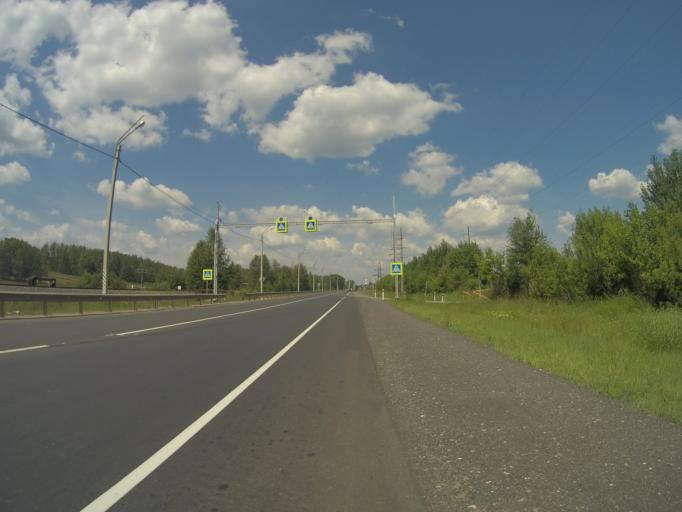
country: RU
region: Kostroma
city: Volgorechensk
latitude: 57.4402
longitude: 41.1712
